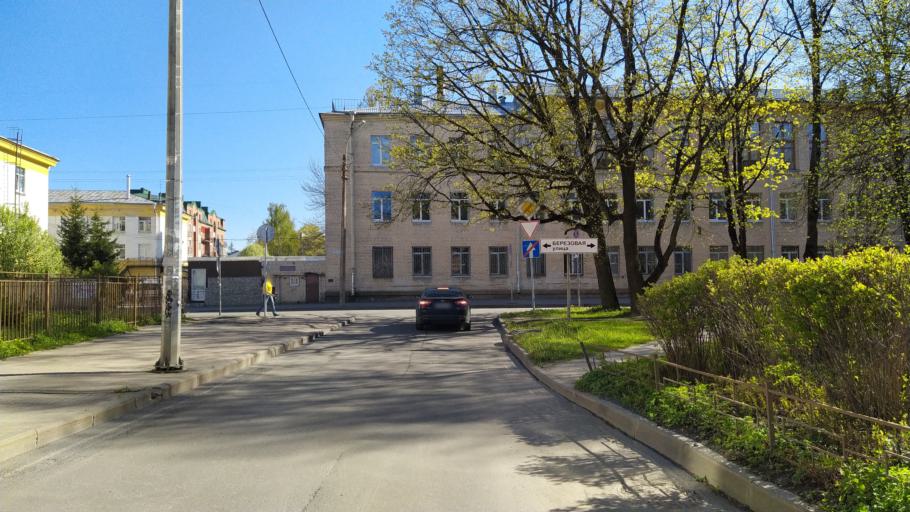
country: RU
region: St.-Petersburg
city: Pavlovsk
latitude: 59.6863
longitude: 30.4283
